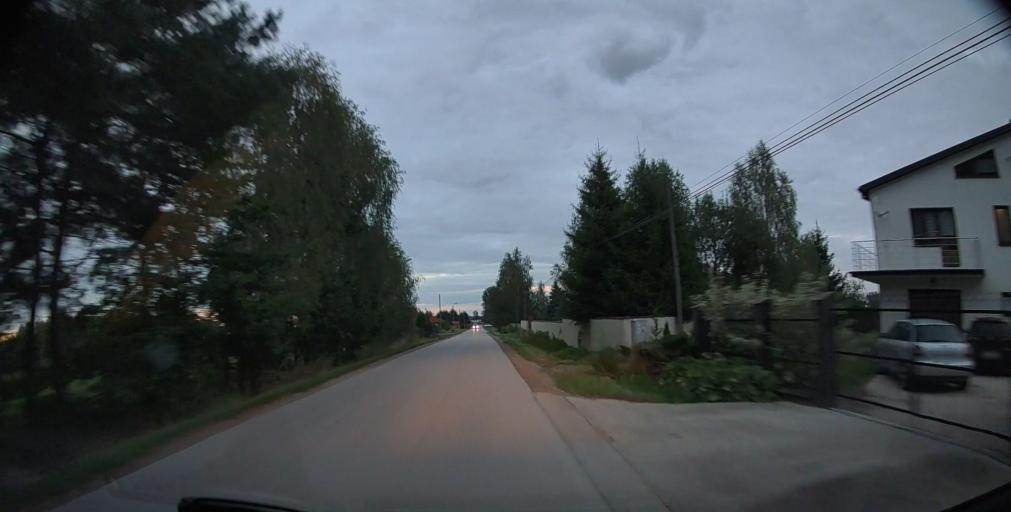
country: PL
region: Masovian Voivodeship
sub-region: Powiat radomski
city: Jedlinsk
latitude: 51.4657
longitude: 21.1285
